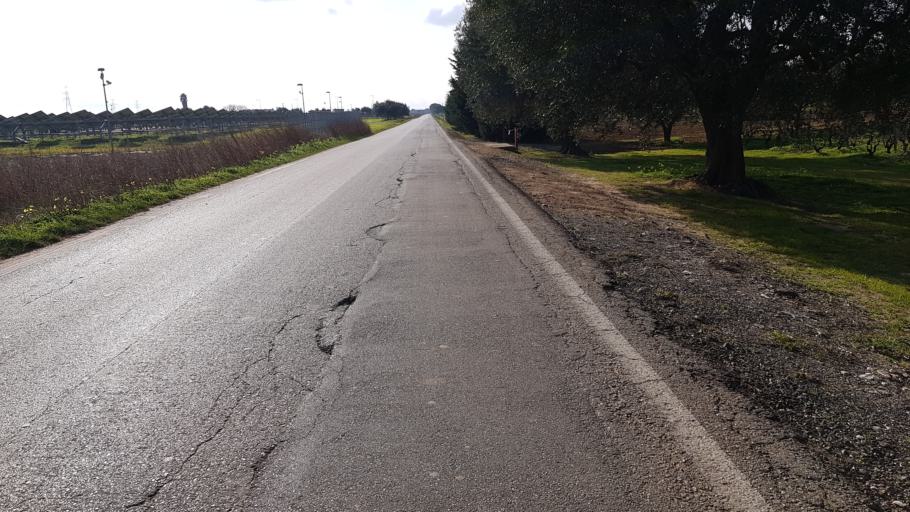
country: IT
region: Apulia
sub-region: Provincia di Brindisi
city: La Rosa
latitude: 40.5850
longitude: 17.9025
